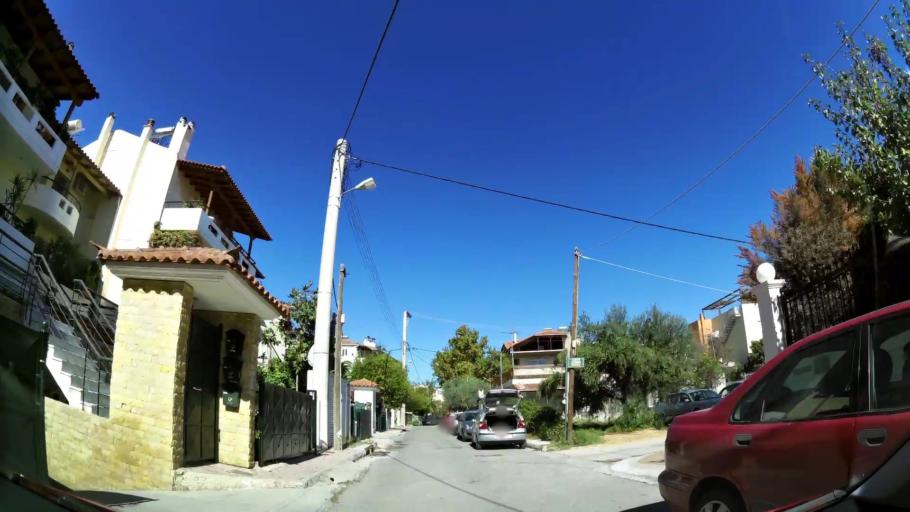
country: GR
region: Attica
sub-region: Nomarchia Anatolikis Attikis
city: Leondarion
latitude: 37.9993
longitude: 23.8594
